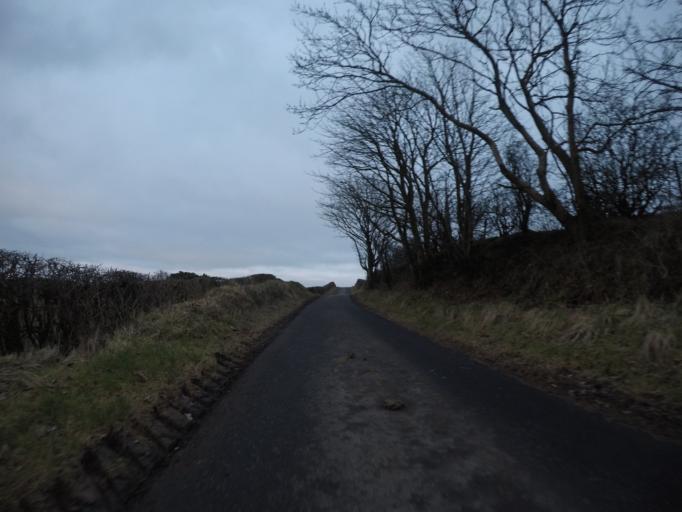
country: GB
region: Scotland
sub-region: North Ayrshire
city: Dalry
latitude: 55.6852
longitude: -4.7328
